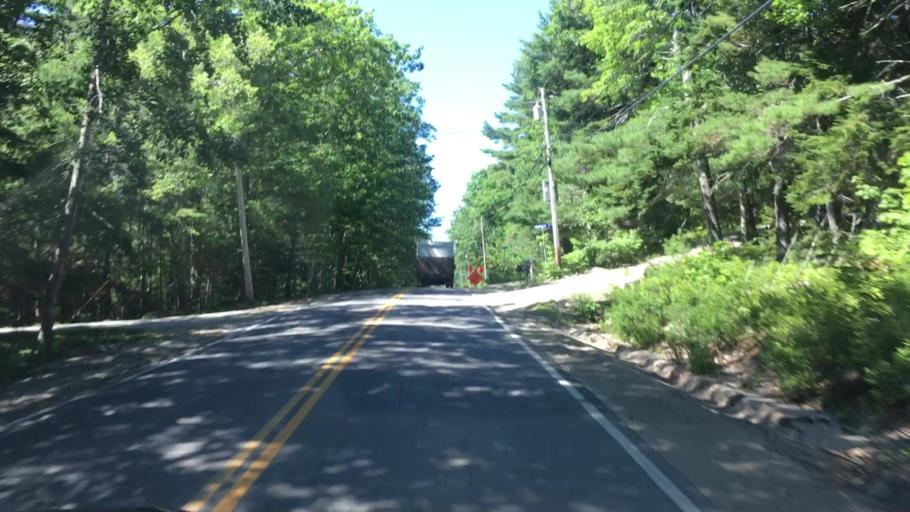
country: US
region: Maine
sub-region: Hancock County
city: Sedgwick
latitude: 44.3649
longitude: -68.5709
